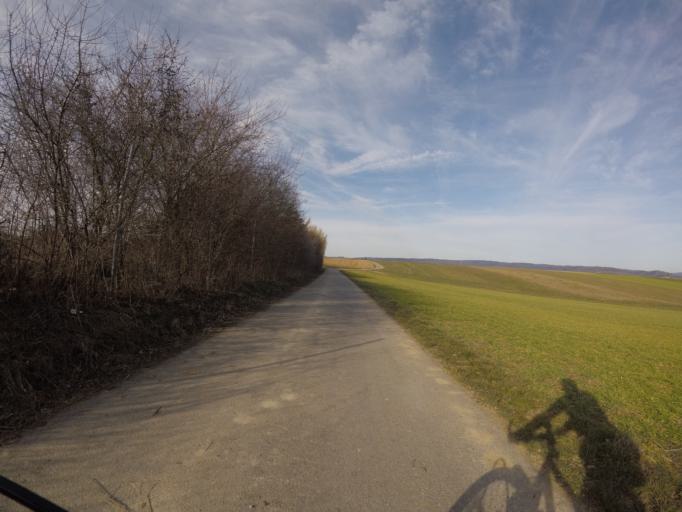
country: DE
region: Baden-Wuerttemberg
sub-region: Regierungsbezirk Stuttgart
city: Mittelschontal
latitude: 48.9554
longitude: 9.3848
